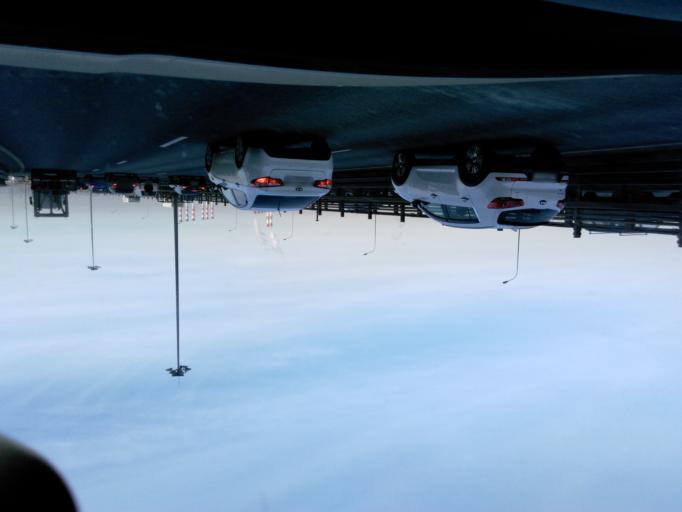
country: RU
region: Moskovskaya
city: Presnenskiy
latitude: 55.7517
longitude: 37.5316
